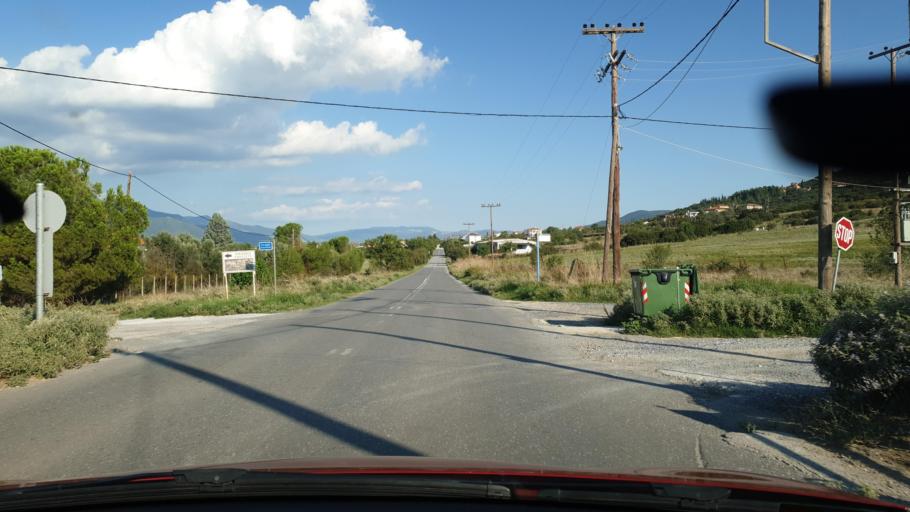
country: GR
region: Central Macedonia
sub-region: Nomos Thessalonikis
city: Agia Paraskevi
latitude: 40.4820
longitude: 23.0614
